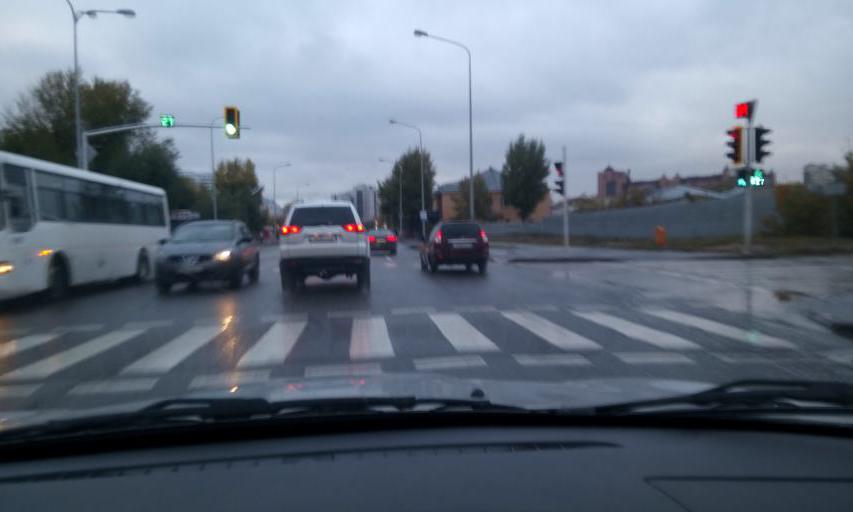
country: KZ
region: Astana Qalasy
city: Astana
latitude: 51.1628
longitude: 71.4532
